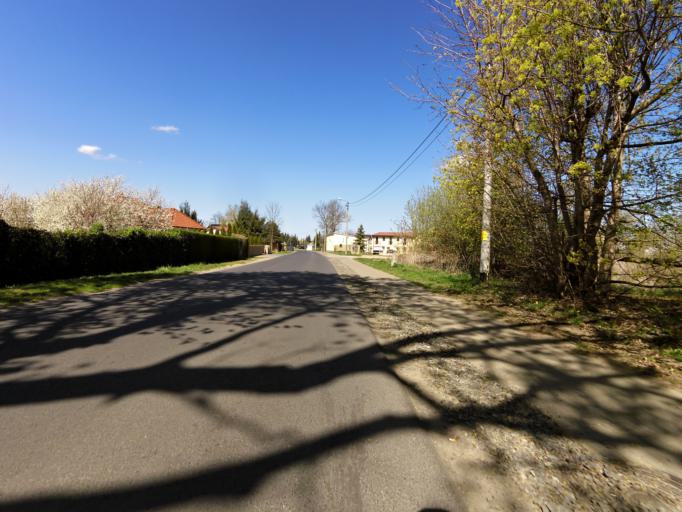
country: PL
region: West Pomeranian Voivodeship
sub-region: Powiat mysliborski
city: Debno
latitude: 52.7310
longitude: 14.6965
